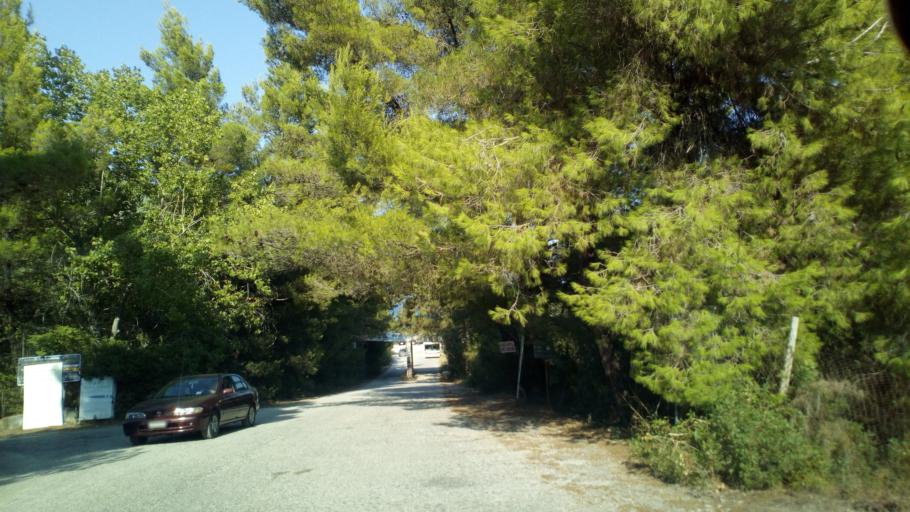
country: GR
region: Central Macedonia
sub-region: Nomos Chalkidikis
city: Pefkochori
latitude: 39.9589
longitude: 23.6745
